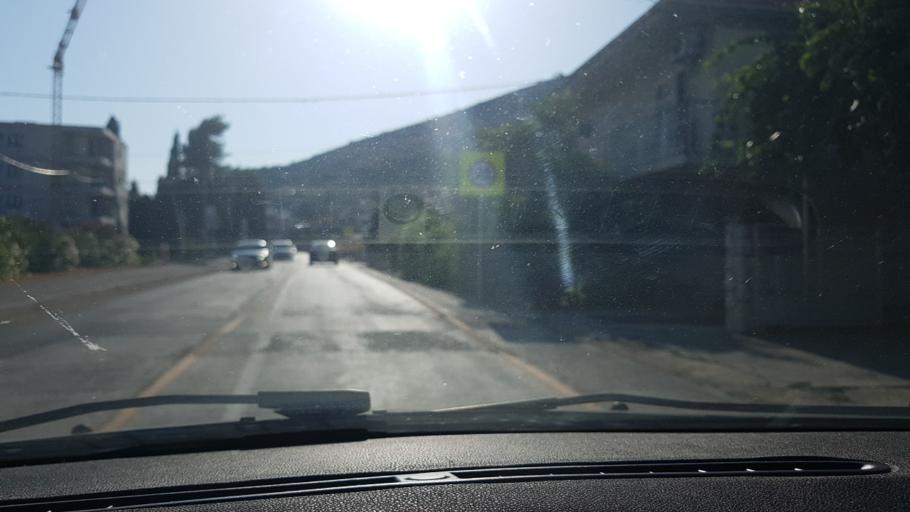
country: HR
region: Splitsko-Dalmatinska
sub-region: Grad Trogir
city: Trogir
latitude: 43.5193
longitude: 16.2265
